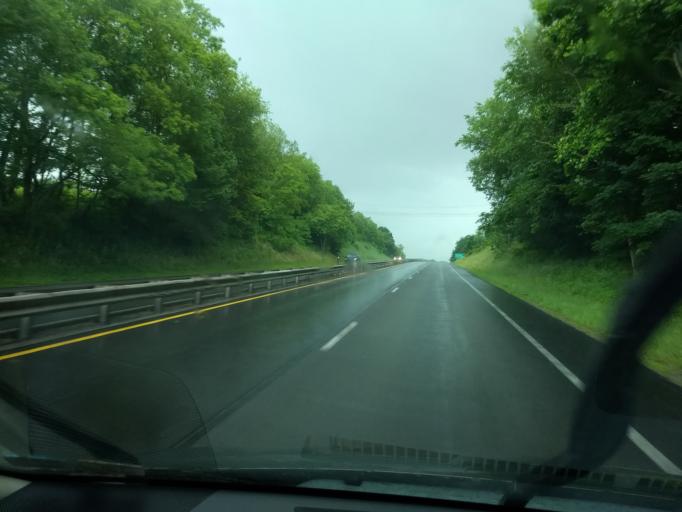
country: US
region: Pennsylvania
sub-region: Armstrong County
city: Apollo
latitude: 40.5296
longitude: -79.6042
